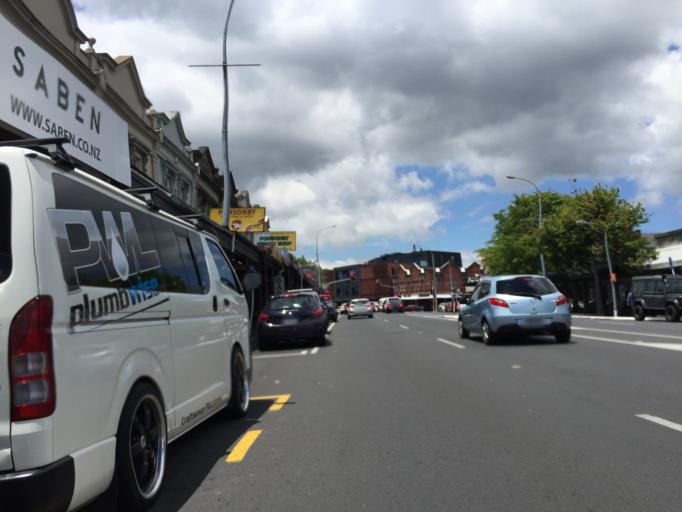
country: NZ
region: Auckland
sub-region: Auckland
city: Auckland
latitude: -36.8552
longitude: 174.7463
